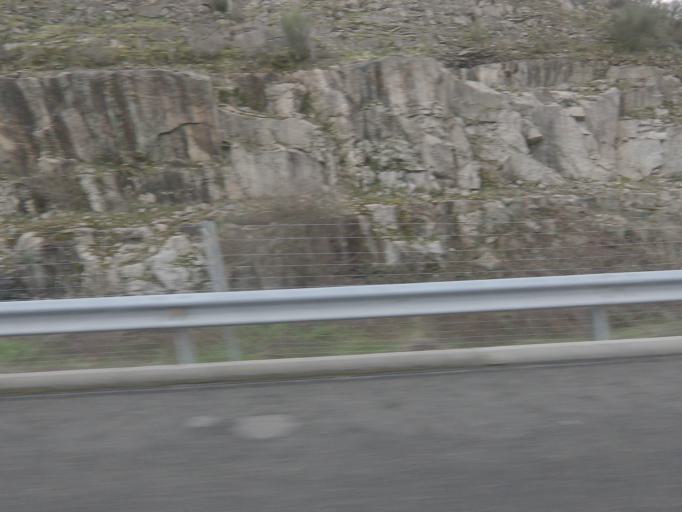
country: ES
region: Galicia
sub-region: Provincia de Ourense
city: Punxin
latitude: 42.3927
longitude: -7.9979
